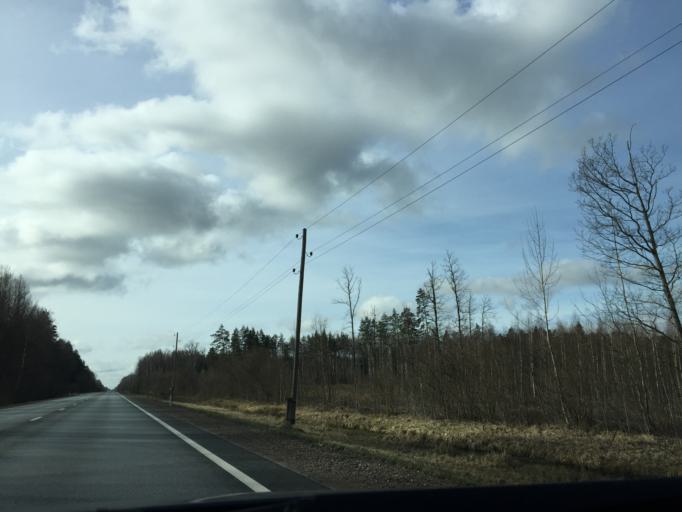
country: LV
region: Jelgava
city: Jelgava
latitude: 56.5587
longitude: 23.7113
